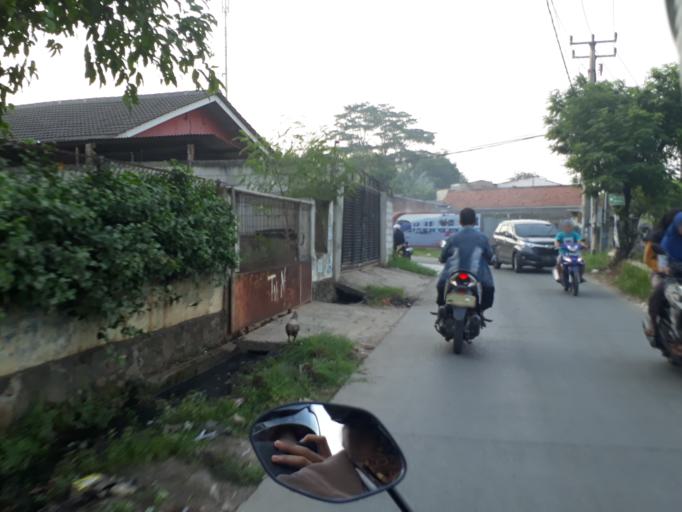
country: ID
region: West Java
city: Bekasi
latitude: -6.2463
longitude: 107.0588
